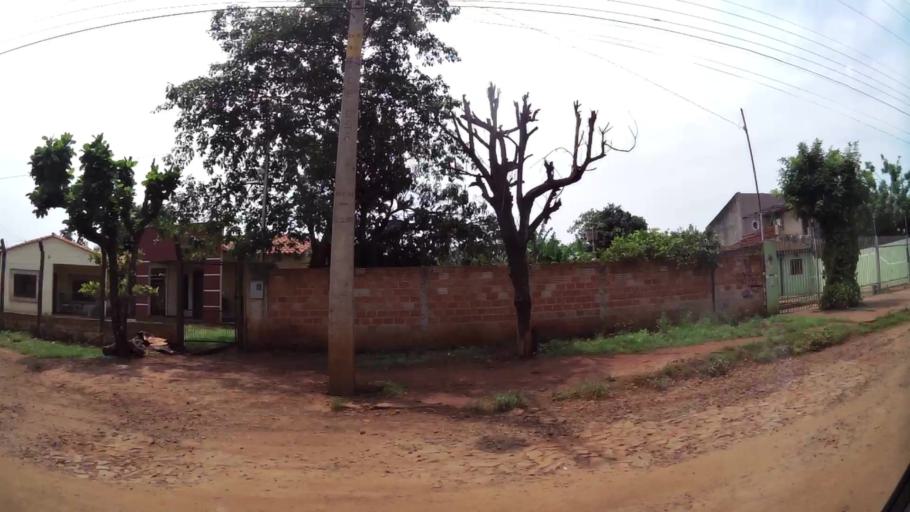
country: PY
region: Alto Parana
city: Ciudad del Este
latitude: -25.4977
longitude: -54.6278
